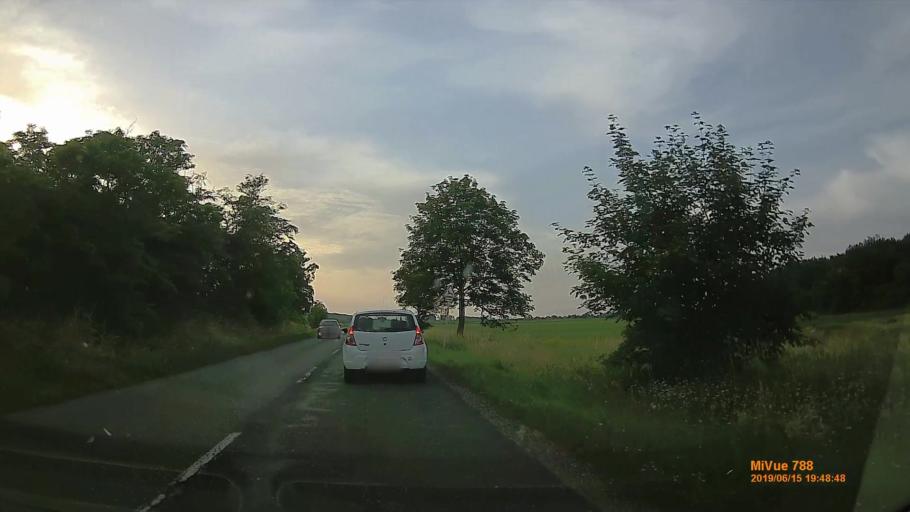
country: HU
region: Veszprem
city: Szentkiralyszabadja
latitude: 47.0281
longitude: 17.9384
